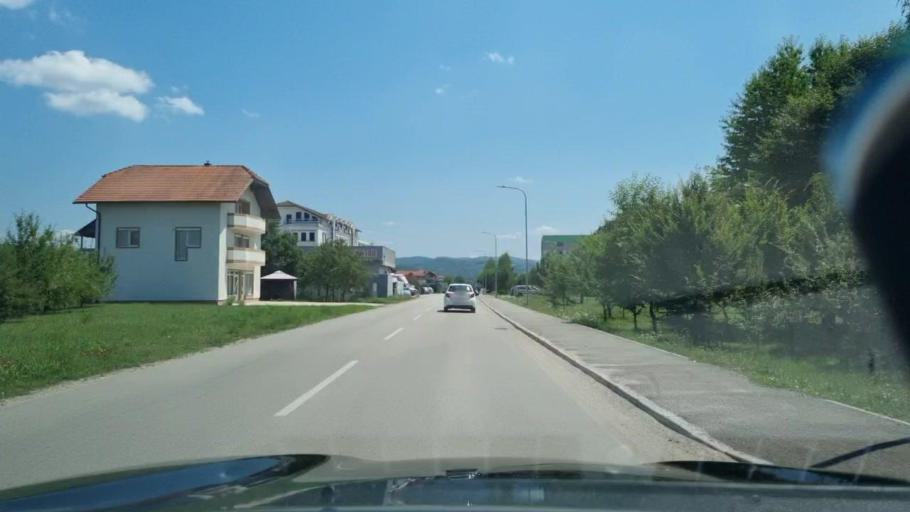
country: BA
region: Federation of Bosnia and Herzegovina
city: Sanski Most
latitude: 44.7711
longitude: 16.6541
